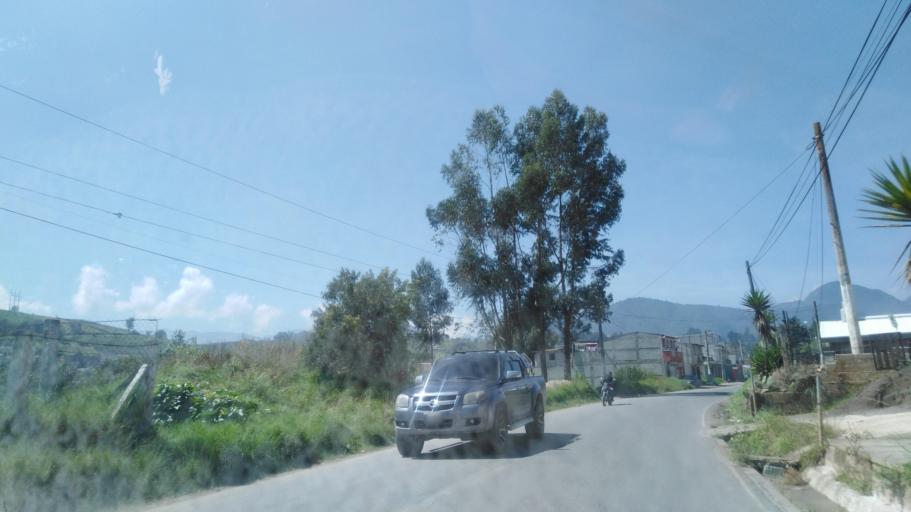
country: GT
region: Quetzaltenango
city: Quetzaltenango
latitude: 14.8569
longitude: -91.4909
